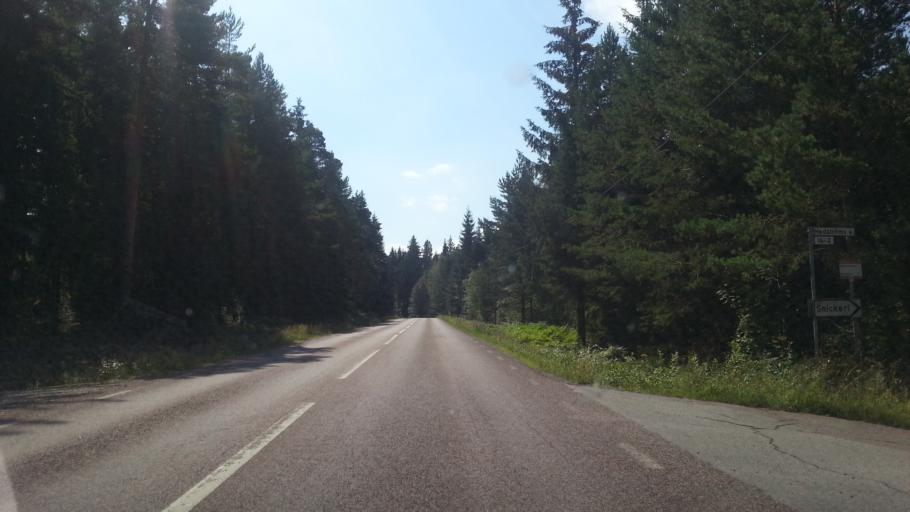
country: SE
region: Dalarna
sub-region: Faluns Kommun
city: Svardsjo
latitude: 60.6485
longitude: 15.7857
